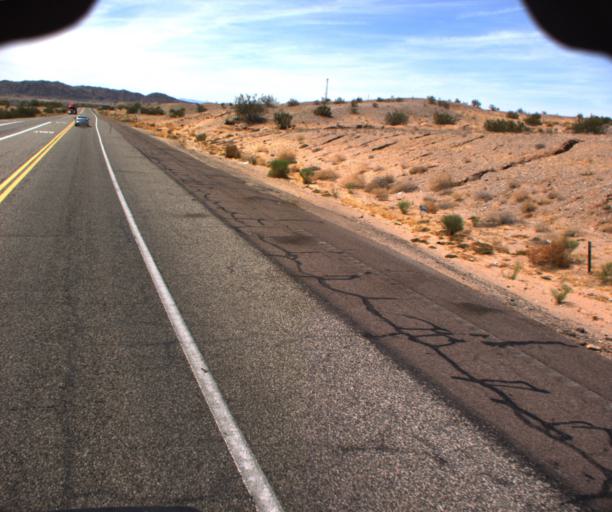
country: US
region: Arizona
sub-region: La Paz County
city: Parker
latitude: 33.9950
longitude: -114.2175
